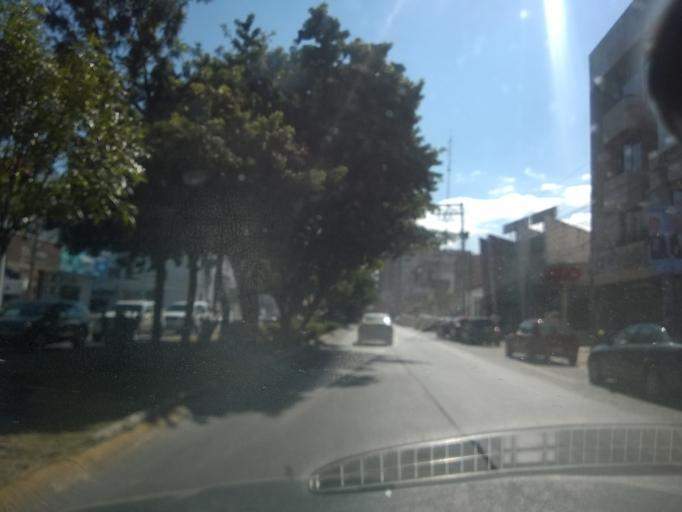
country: MX
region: Guanajuato
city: Leon
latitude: 21.1490
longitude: -101.6899
